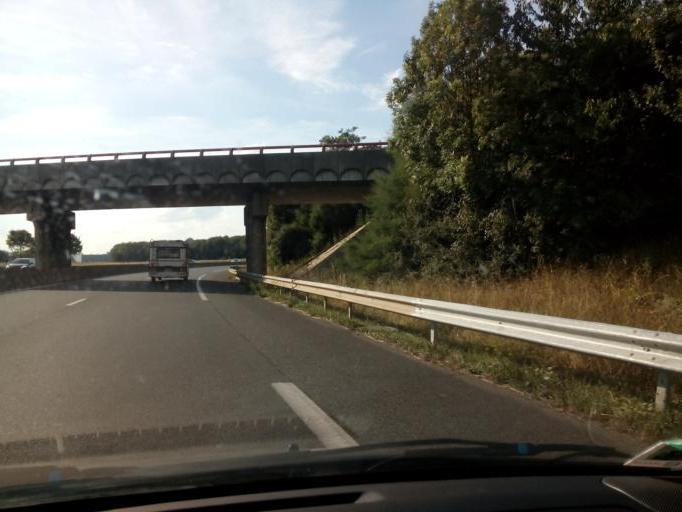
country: FR
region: Centre
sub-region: Departement d'Indre-et-Loire
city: Joue-les-Tours
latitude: 47.3311
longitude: 0.6745
